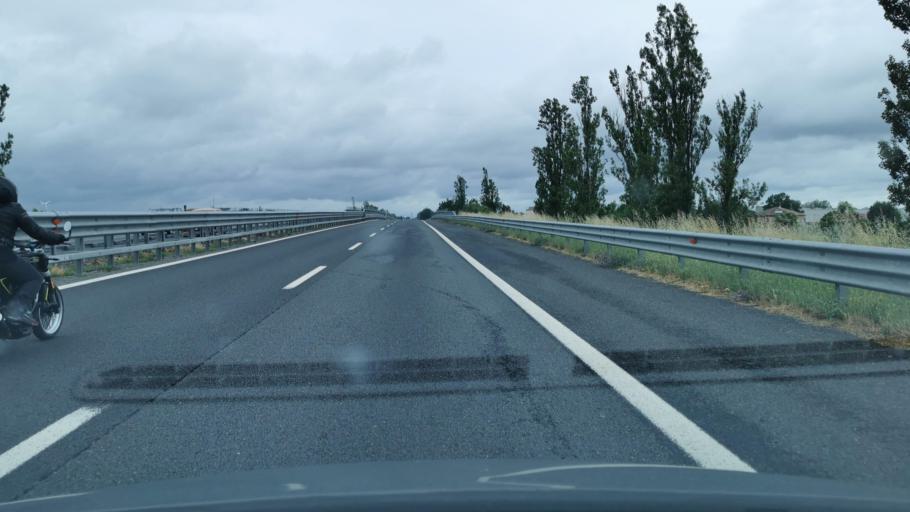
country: IT
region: Emilia-Romagna
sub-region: Provincia di Ravenna
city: Bagnacavallo
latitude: 44.4069
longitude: 12.0044
